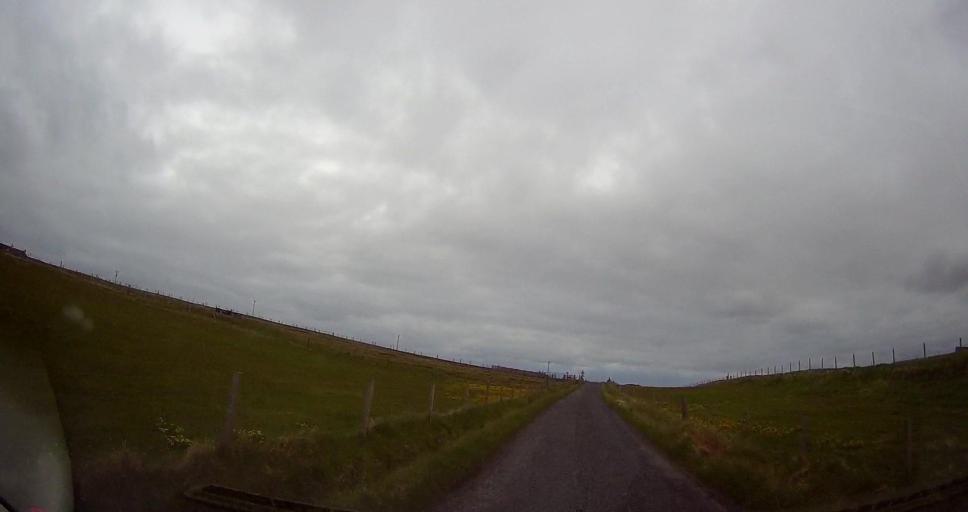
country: GB
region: Scotland
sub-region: Shetland Islands
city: Shetland
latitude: 60.8000
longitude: -0.8736
